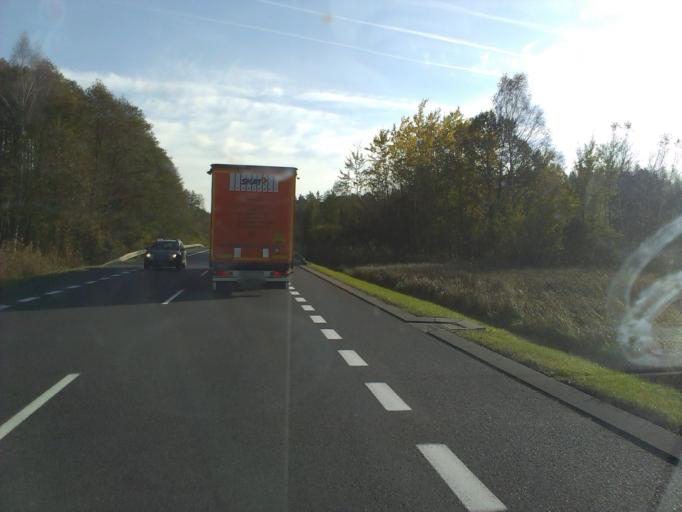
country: PL
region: Lubusz
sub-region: Powiat nowosolski
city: Nowa Sol
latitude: 51.7557
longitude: 15.6914
